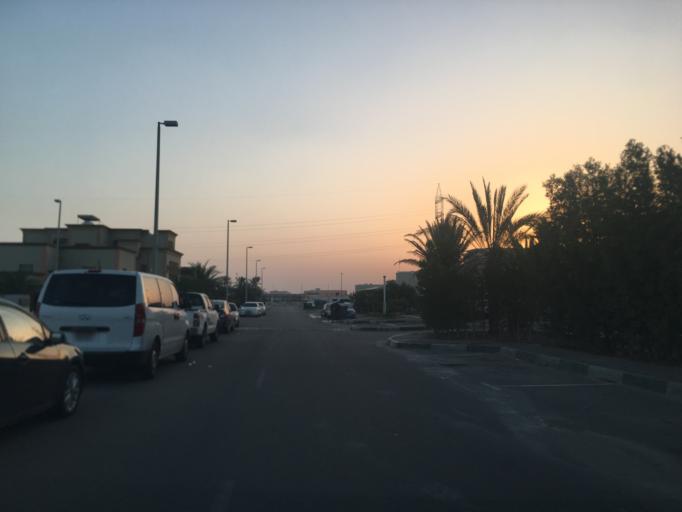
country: AE
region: Abu Dhabi
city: Abu Dhabi
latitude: 24.3095
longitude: 54.6397
